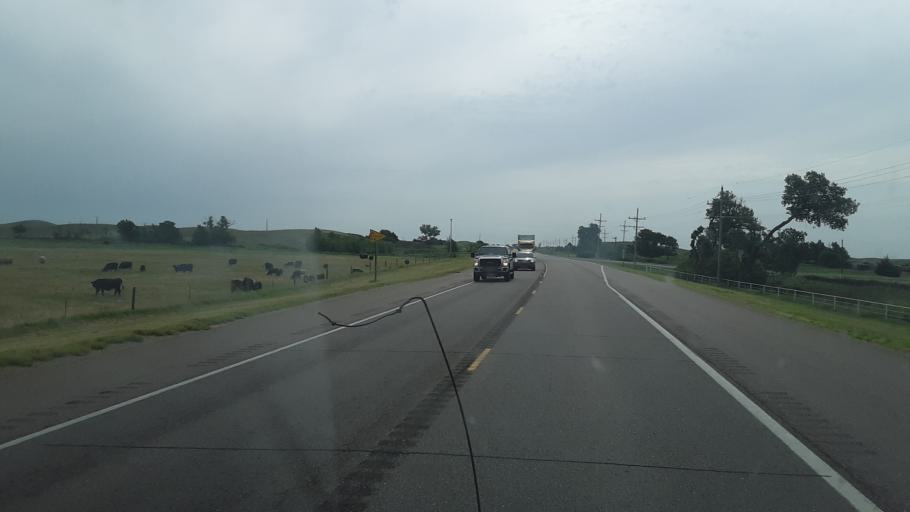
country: US
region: Kansas
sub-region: Edwards County
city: Kinsley
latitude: 37.9279
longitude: -99.3714
